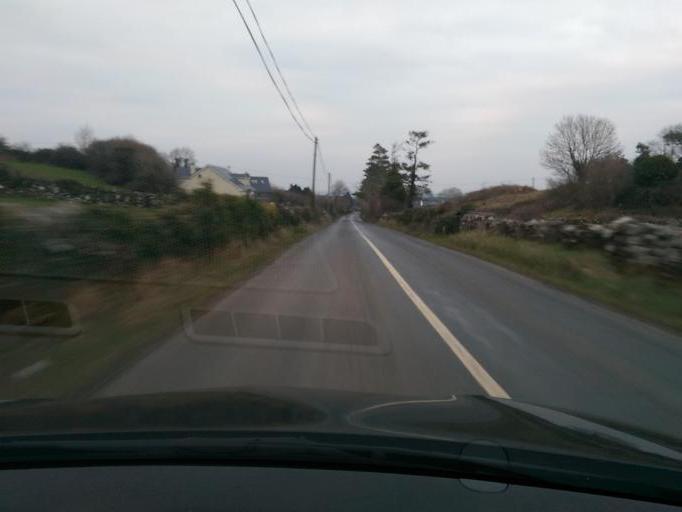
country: IE
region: Connaught
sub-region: County Galway
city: Moycullen
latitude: 53.3026
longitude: -9.1566
